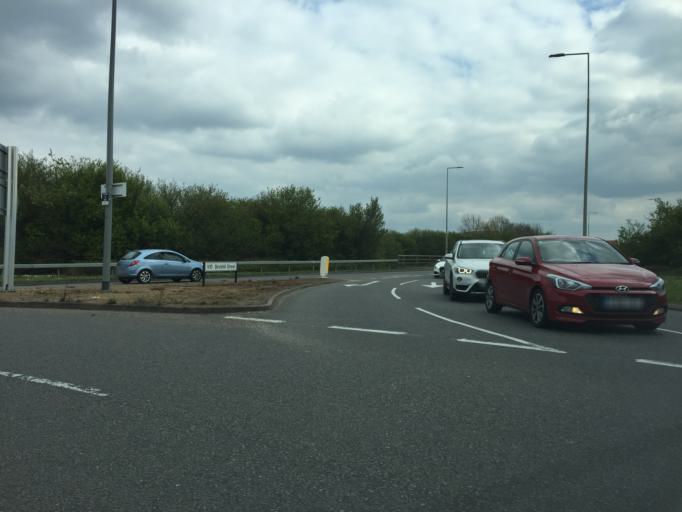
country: GB
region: England
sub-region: Milton Keynes
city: Broughton
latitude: 52.0374
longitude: -0.7096
